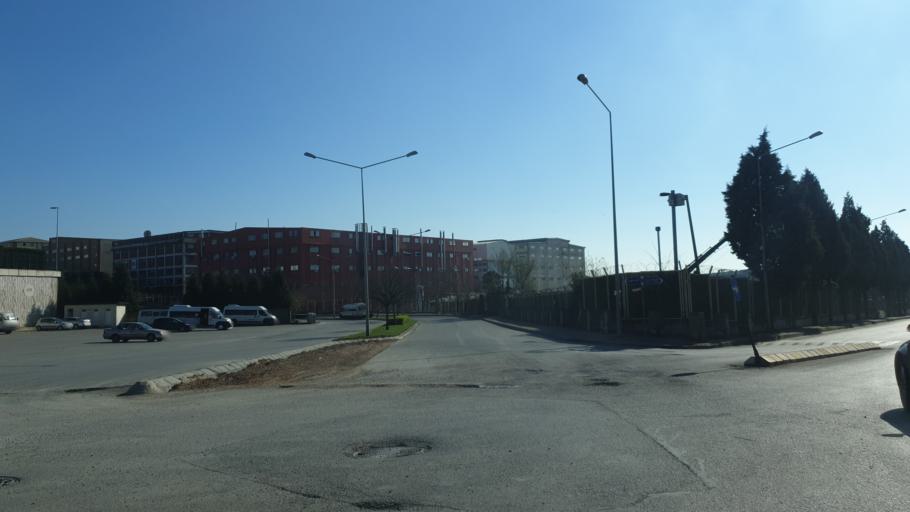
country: TR
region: Kocaeli
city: Balcik
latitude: 40.8790
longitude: 29.3716
